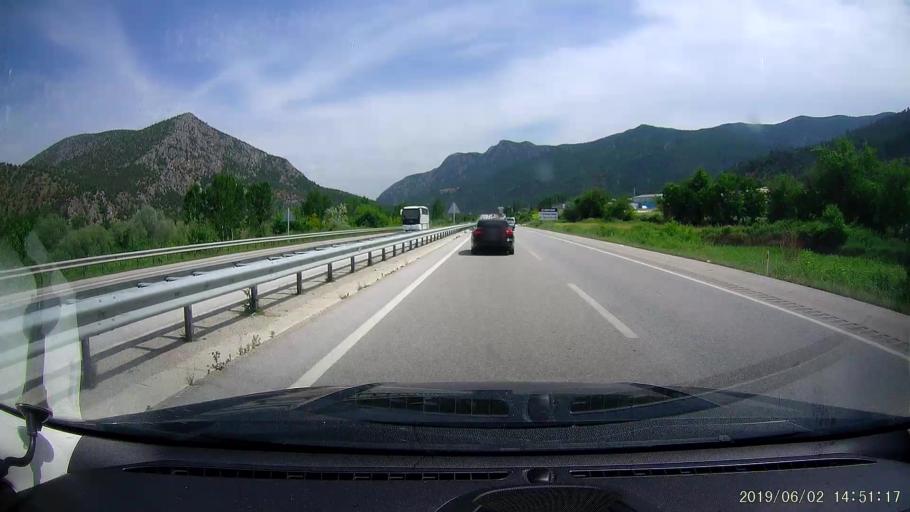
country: TR
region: Corum
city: Kargi
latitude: 41.0625
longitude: 34.5378
